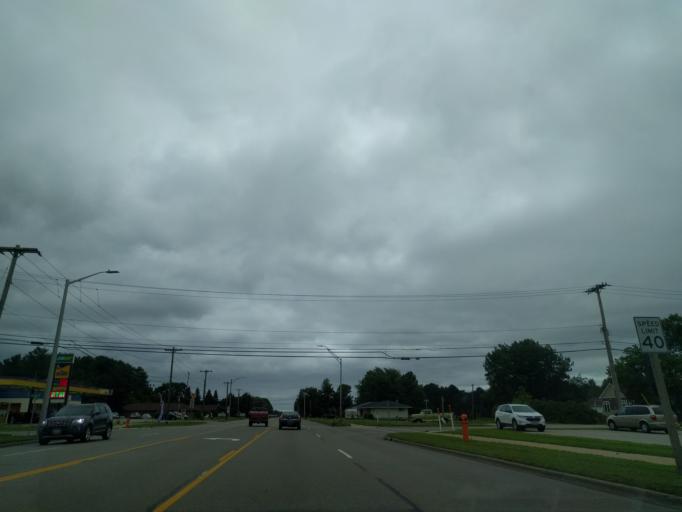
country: US
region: Michigan
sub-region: Delta County
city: Escanaba
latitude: 45.7359
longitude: -87.0799
